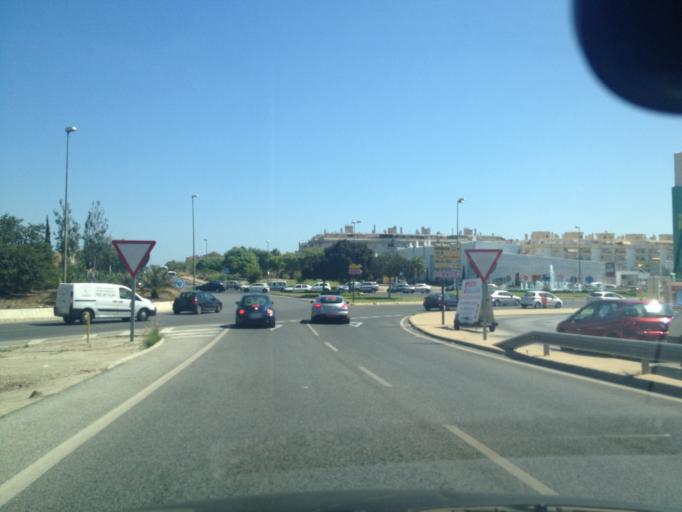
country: ES
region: Andalusia
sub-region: Provincia de Malaga
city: Malaga
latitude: 36.7126
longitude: -4.4673
